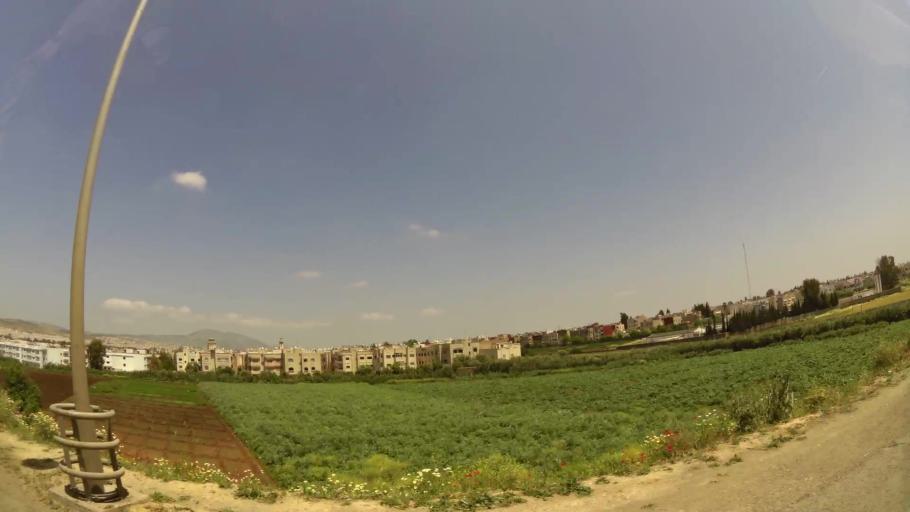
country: MA
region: Fes-Boulemane
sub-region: Fes
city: Fes
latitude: 34.0337
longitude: -5.0311
